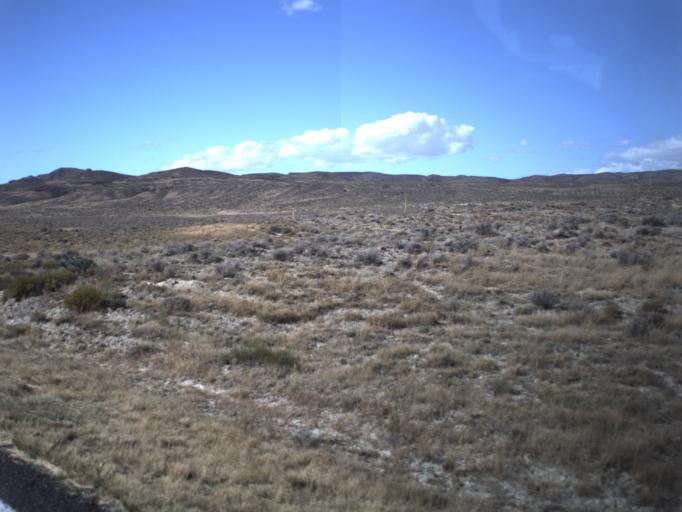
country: US
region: Utah
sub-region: Millard County
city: Fillmore
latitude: 38.8917
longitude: -112.8269
